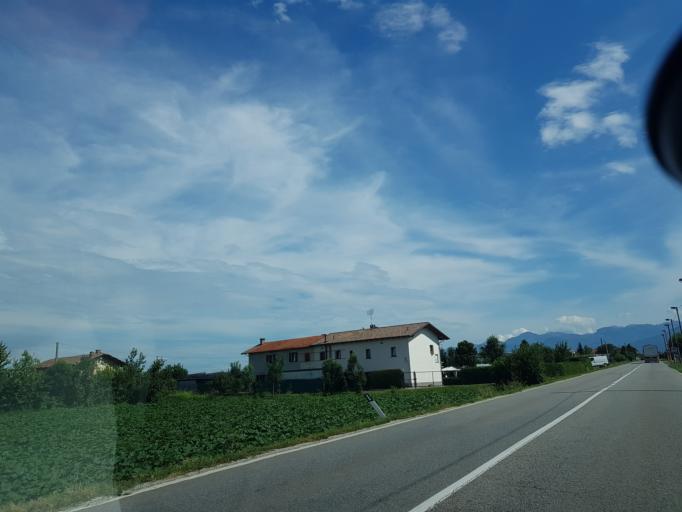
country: IT
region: Piedmont
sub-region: Provincia di Cuneo
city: Roata Rossi
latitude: 44.4416
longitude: 7.5315
